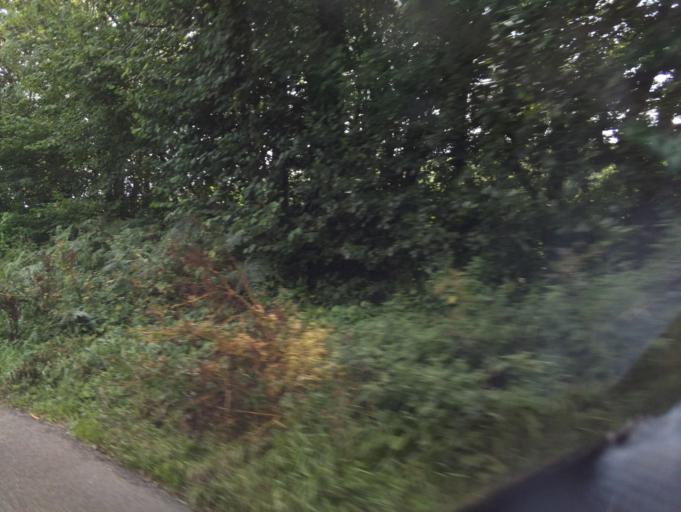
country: GB
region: England
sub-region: Devon
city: Totnes
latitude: 50.4294
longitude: -3.7304
